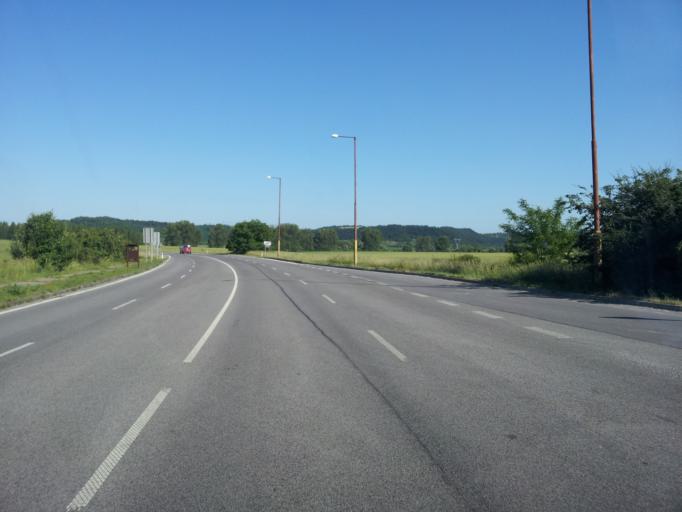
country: SK
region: Nitriansky
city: Sahy
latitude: 48.0821
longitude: 18.9442
